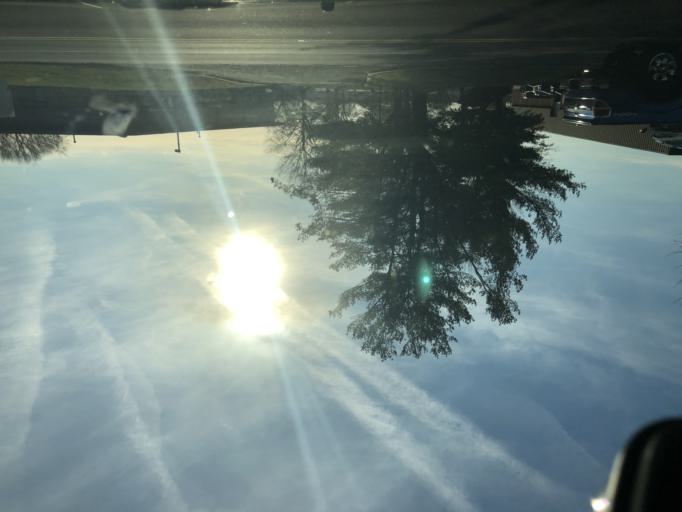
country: US
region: New Jersey
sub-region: Burlington County
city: Cinnaminson
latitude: 39.9790
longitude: -74.9902
